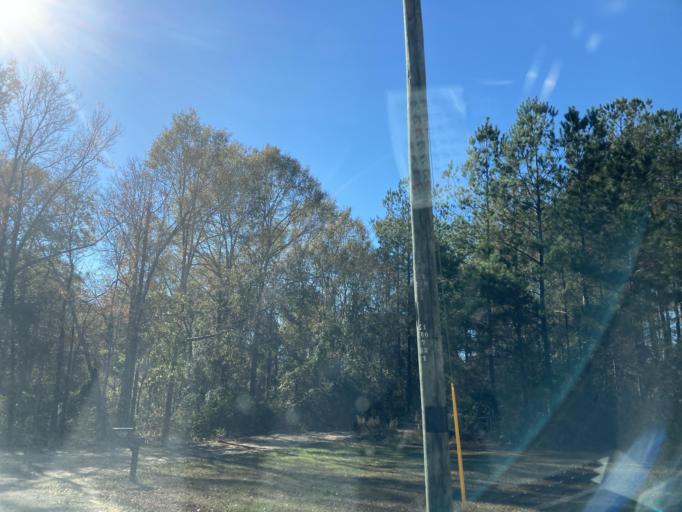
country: US
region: Mississippi
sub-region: Lamar County
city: Sumrall
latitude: 31.2934
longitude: -89.6469
